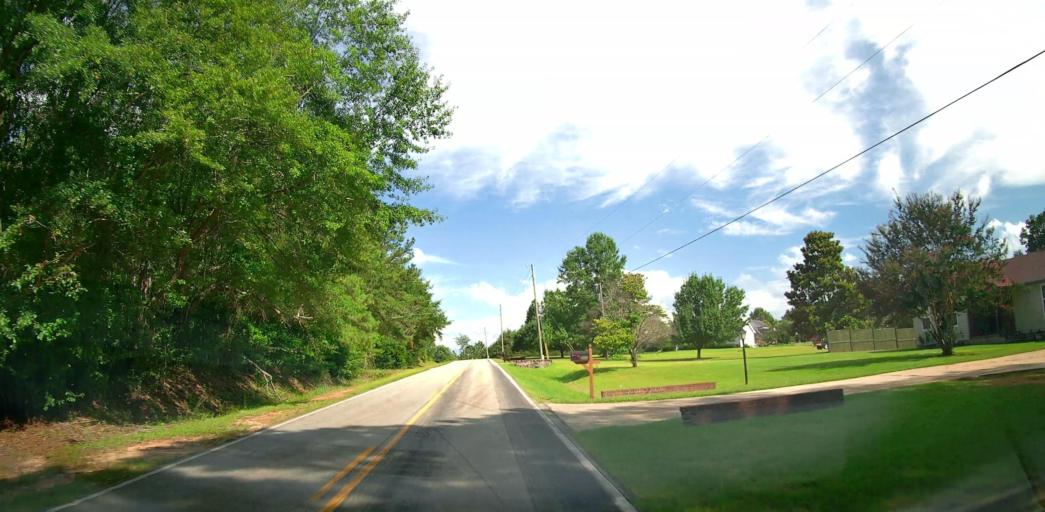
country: US
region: Georgia
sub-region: Houston County
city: Robins Air Force Base
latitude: 32.5349
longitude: -83.6429
